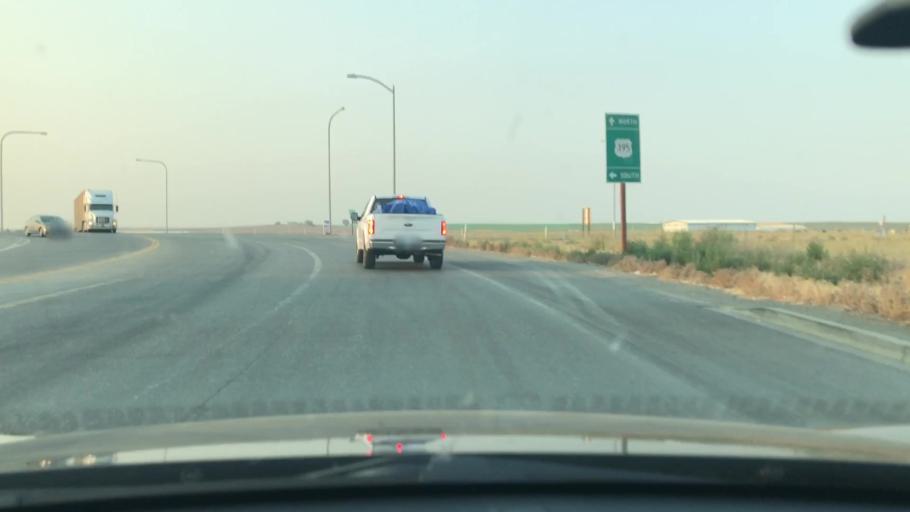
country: US
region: Washington
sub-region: Franklin County
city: Pasco
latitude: 46.2642
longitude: -119.0837
